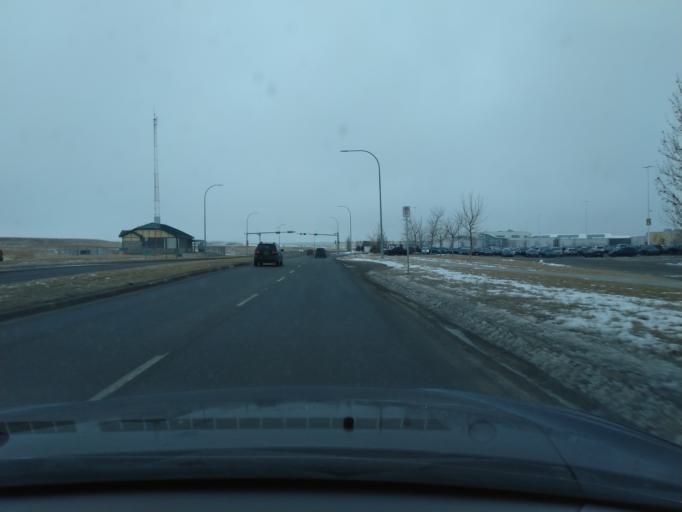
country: CA
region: Alberta
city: Airdrie
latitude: 51.2069
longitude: -113.9904
